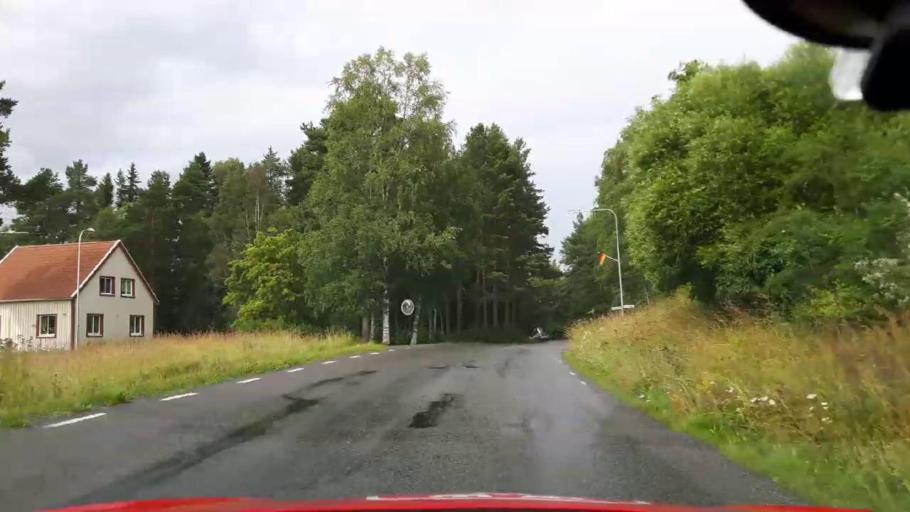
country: SE
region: Jaemtland
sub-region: Krokoms Kommun
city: Krokom
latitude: 63.3465
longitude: 14.2604
